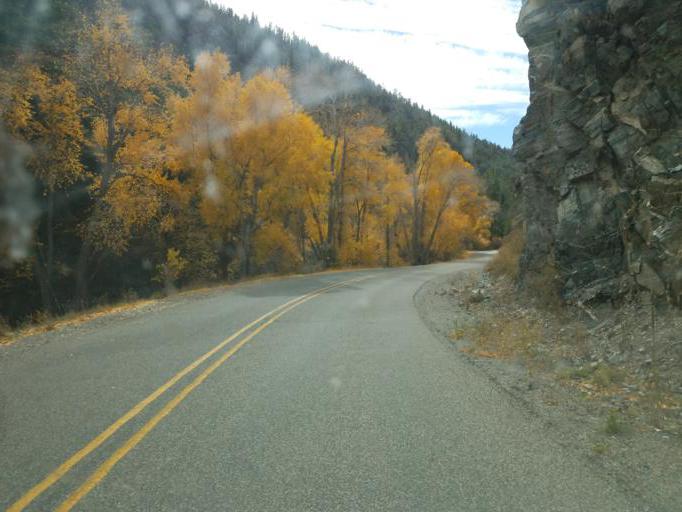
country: US
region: New Mexico
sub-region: Taos County
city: Arroyo Seco
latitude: 36.5465
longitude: -105.5523
